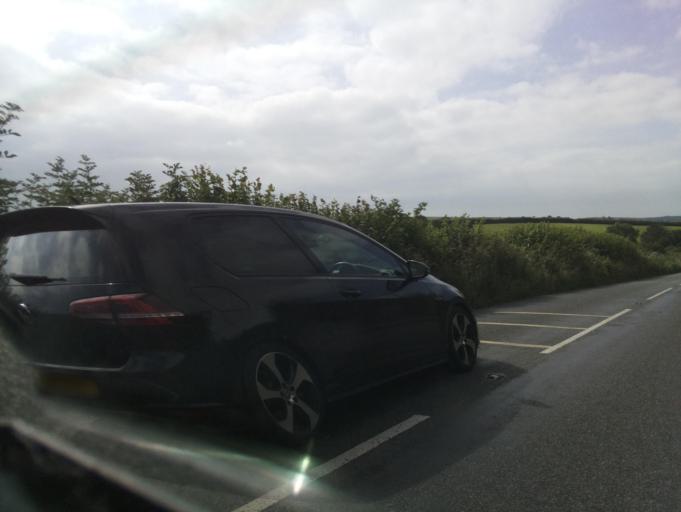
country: GB
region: England
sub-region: Devon
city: Dartmouth
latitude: 50.3666
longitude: -3.5496
